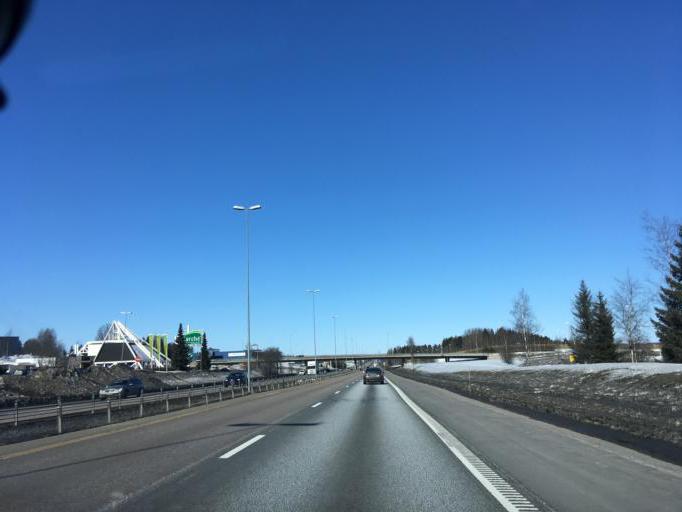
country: NO
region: Akershus
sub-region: Ullensaker
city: Klofta
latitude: 60.0777
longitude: 11.1514
